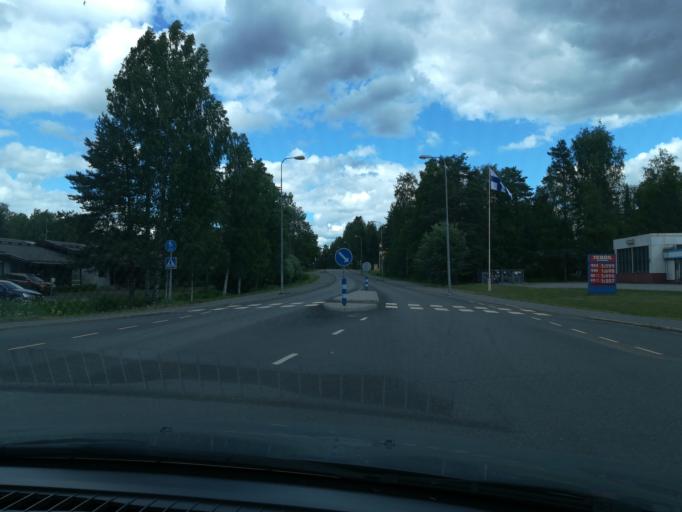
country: FI
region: Southern Savonia
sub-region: Mikkeli
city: Maentyharju
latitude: 61.4196
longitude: 26.8896
